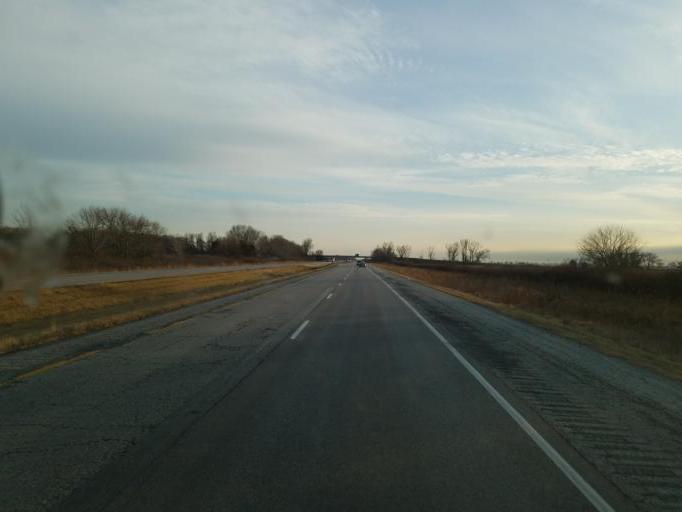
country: US
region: Nebraska
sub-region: Burt County
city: Tekamah
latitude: 41.7345
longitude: -96.0484
